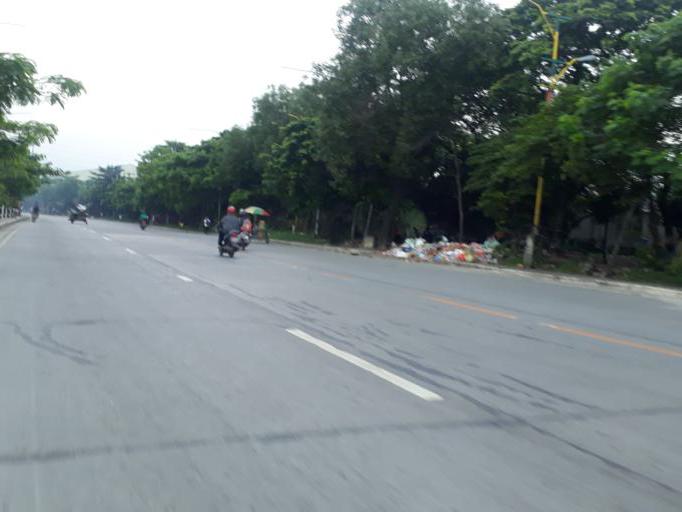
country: PH
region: Metro Manila
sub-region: Caloocan City
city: Niugan
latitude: 14.6476
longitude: 120.9504
